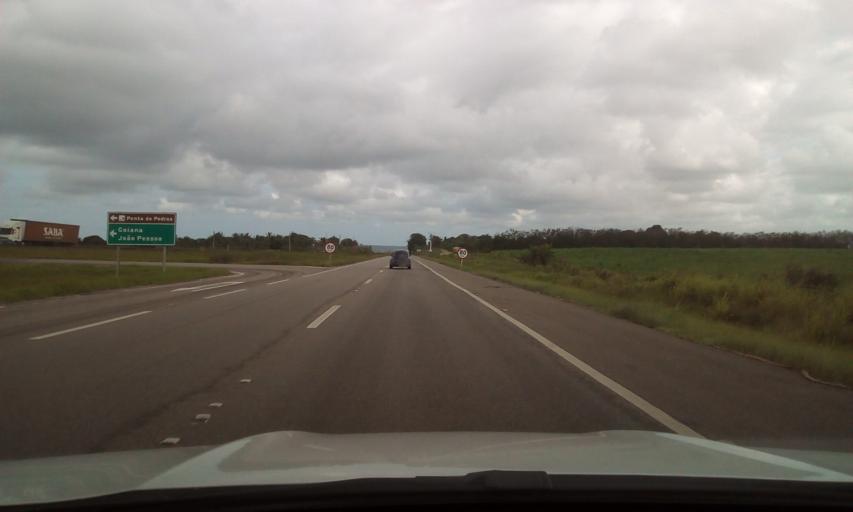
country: BR
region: Pernambuco
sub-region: Itapissuma
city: Itapissuma
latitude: -7.6748
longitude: -34.9294
